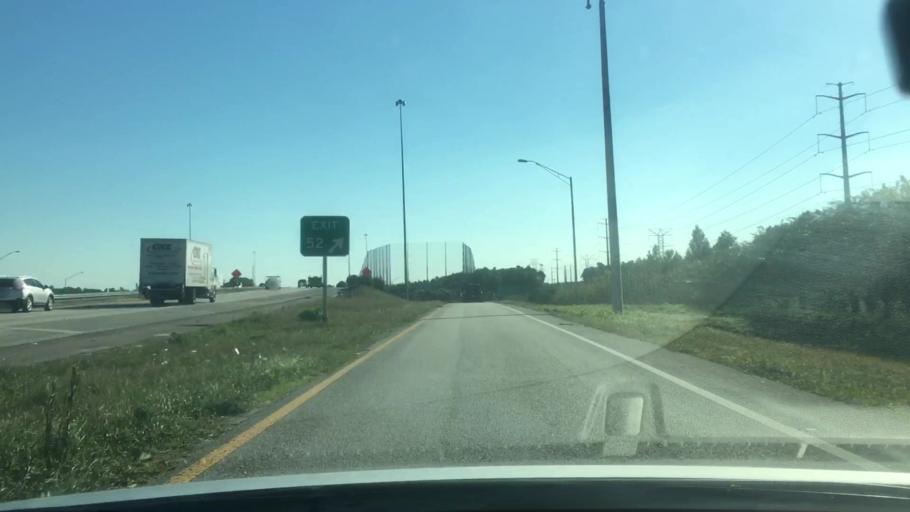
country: US
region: Florida
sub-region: Duval County
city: Jacksonville Beach
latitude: 30.2724
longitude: -81.5215
